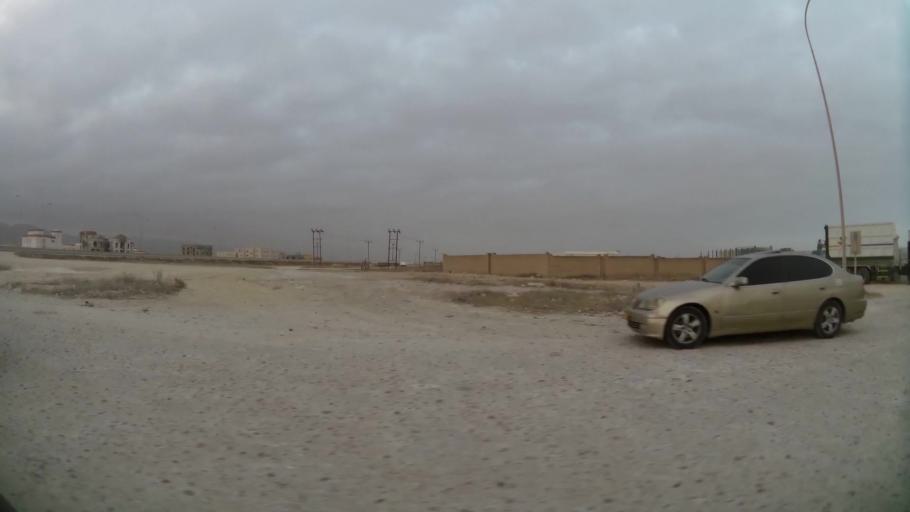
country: OM
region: Zufar
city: Salalah
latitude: 17.0367
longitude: 54.0420
